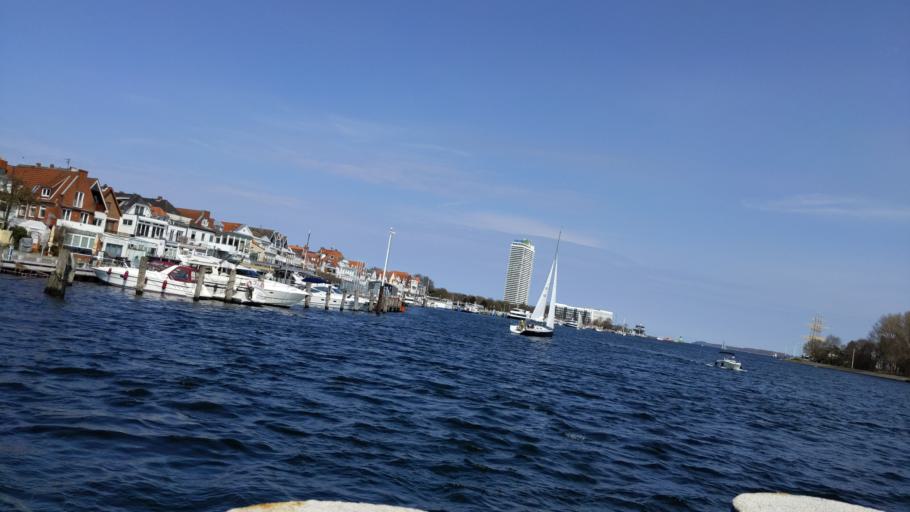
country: DE
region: Schleswig-Holstein
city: Travemuende
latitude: 53.9555
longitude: 10.8684
